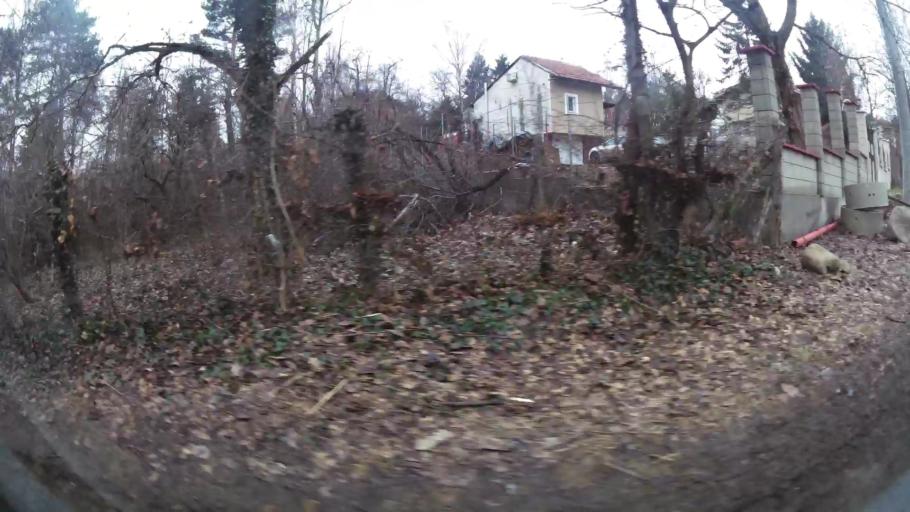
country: BG
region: Sofia-Capital
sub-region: Stolichna Obshtina
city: Sofia
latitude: 42.6122
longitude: 23.3670
